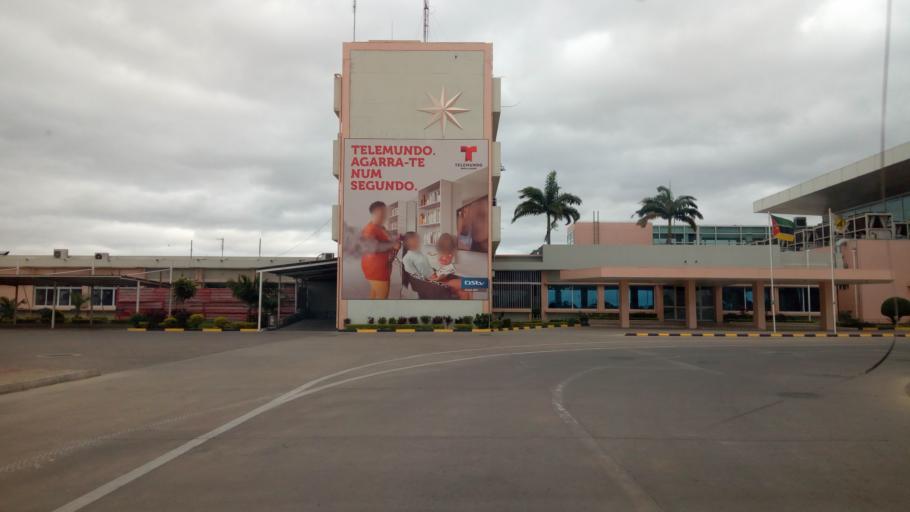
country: MZ
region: Maputo City
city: Maputo
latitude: -25.9254
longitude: 32.5742
